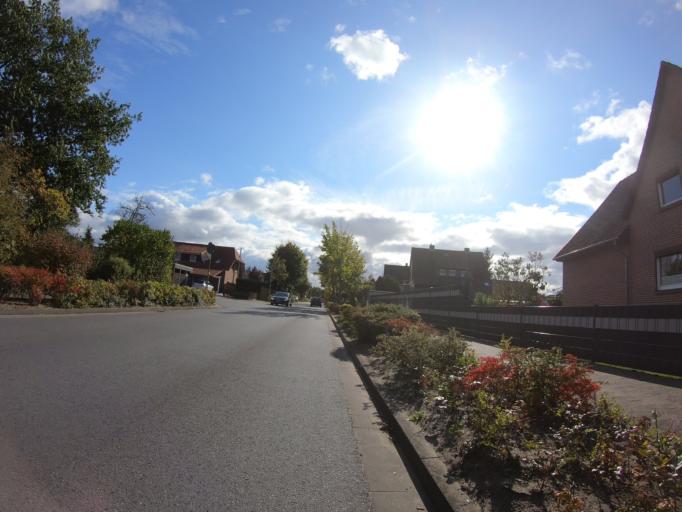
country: DE
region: Lower Saxony
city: Isenbuttel
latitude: 52.4419
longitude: 10.5710
